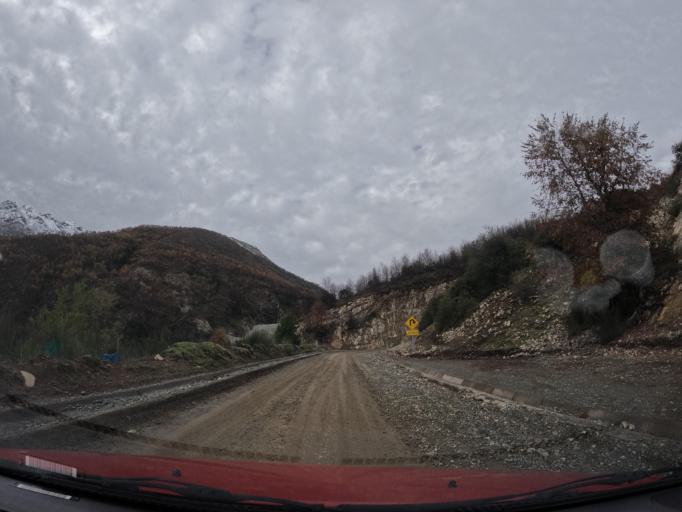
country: CL
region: Maule
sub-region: Provincia de Linares
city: Colbun
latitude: -35.8550
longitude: -71.1880
